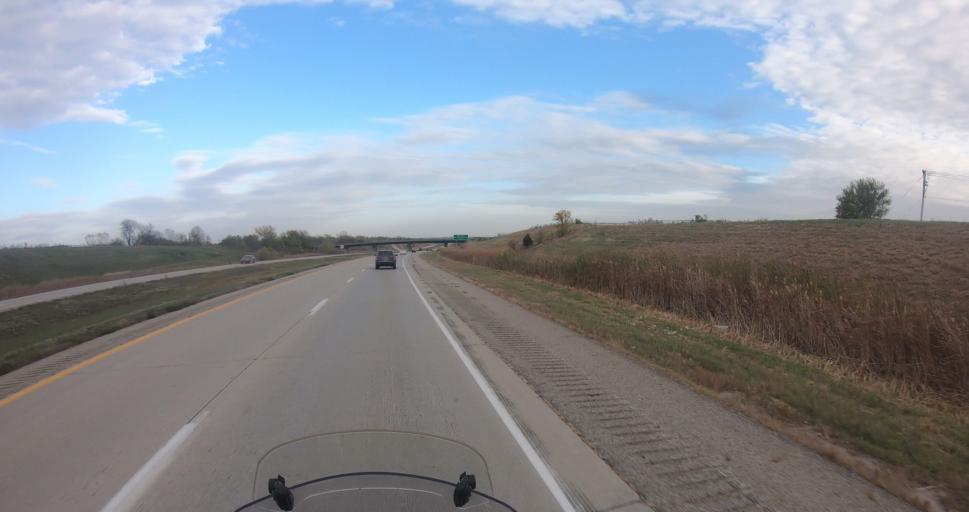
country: US
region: Iowa
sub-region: Warren County
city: Norwalk
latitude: 41.5124
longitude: -93.6568
